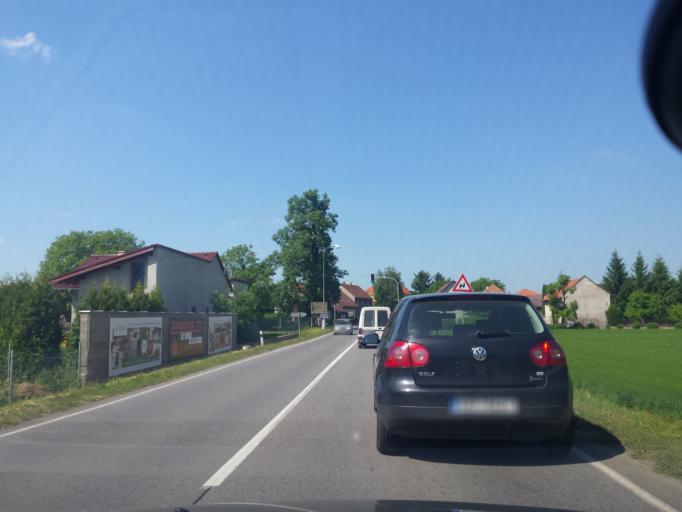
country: CZ
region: Central Bohemia
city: Velke Prilepy
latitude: 50.1887
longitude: 14.3211
